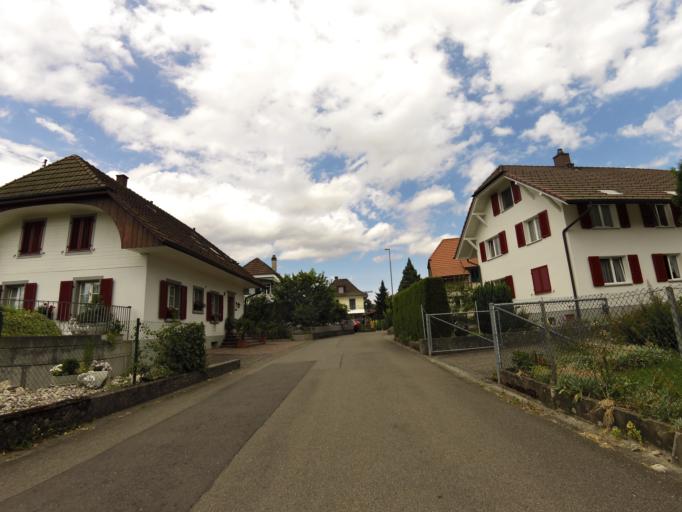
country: CH
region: Bern
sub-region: Oberaargau
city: Aarwangen
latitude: 47.2350
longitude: 7.7813
